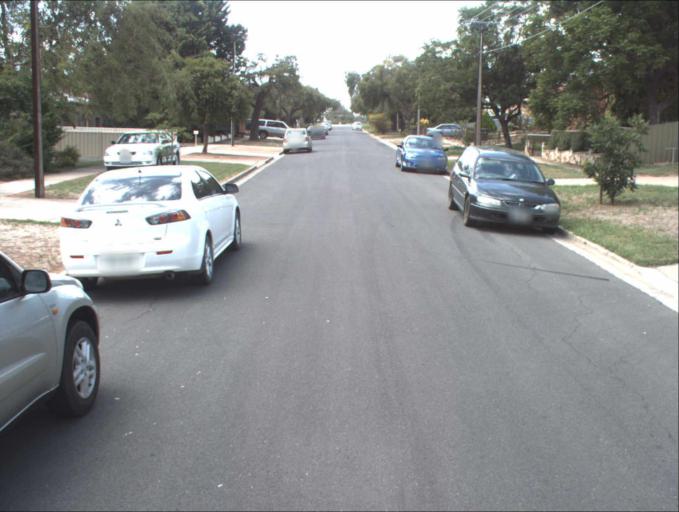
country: AU
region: South Australia
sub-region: Port Adelaide Enfield
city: Enfield
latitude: -34.8519
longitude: 138.6060
